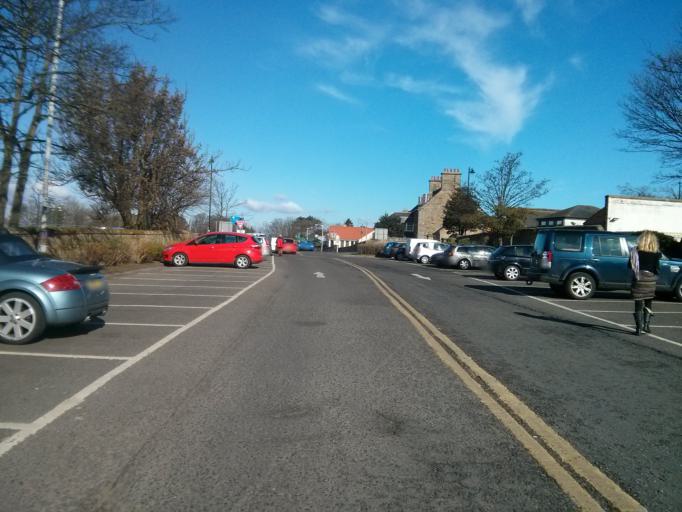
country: GB
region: Scotland
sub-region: Fife
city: Saint Andrews
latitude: 56.3391
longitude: -2.8023
